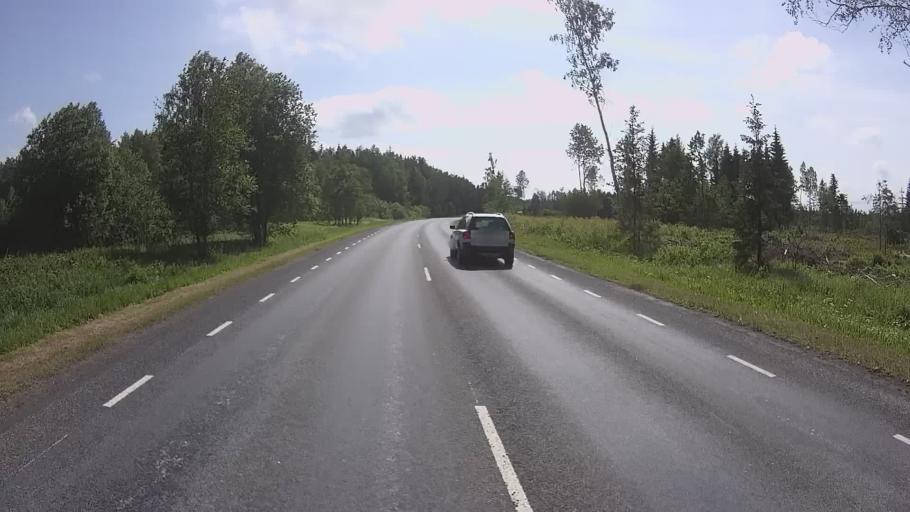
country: EE
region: Tartu
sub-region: UElenurme vald
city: Ulenurme
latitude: 58.2688
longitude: 26.7679
